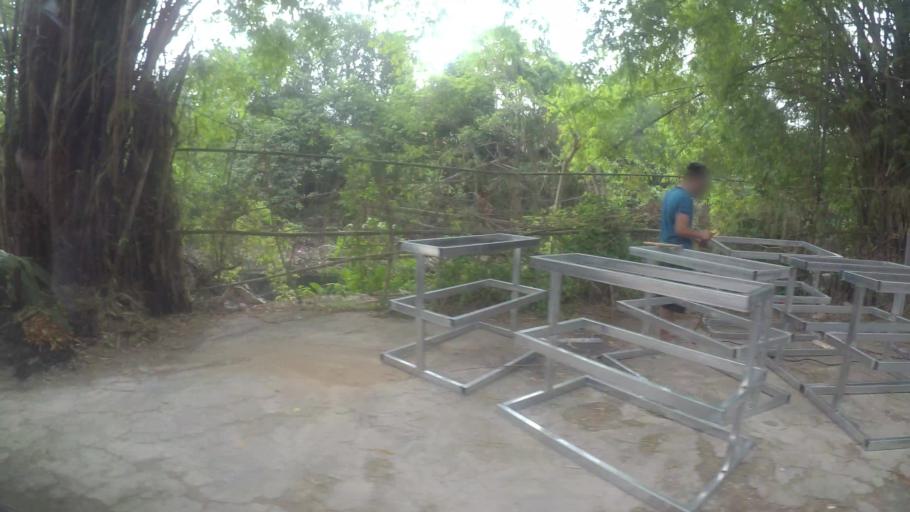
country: VN
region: Ha Noi
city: Ha Dong
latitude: 20.9708
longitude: 105.7637
